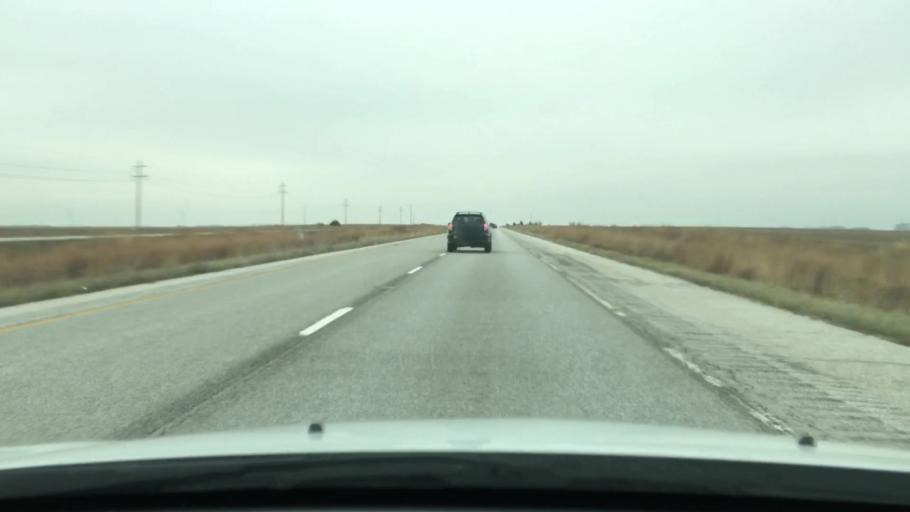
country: US
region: Illinois
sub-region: Morgan County
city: Jacksonville
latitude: 39.7378
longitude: -90.1209
